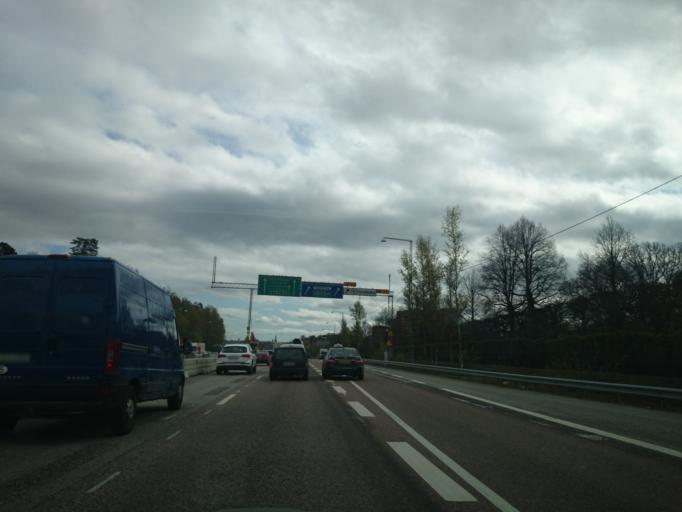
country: SE
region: Stockholm
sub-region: Norrtalje Kommun
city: Bergshamra
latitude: 59.3575
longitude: 18.0309
